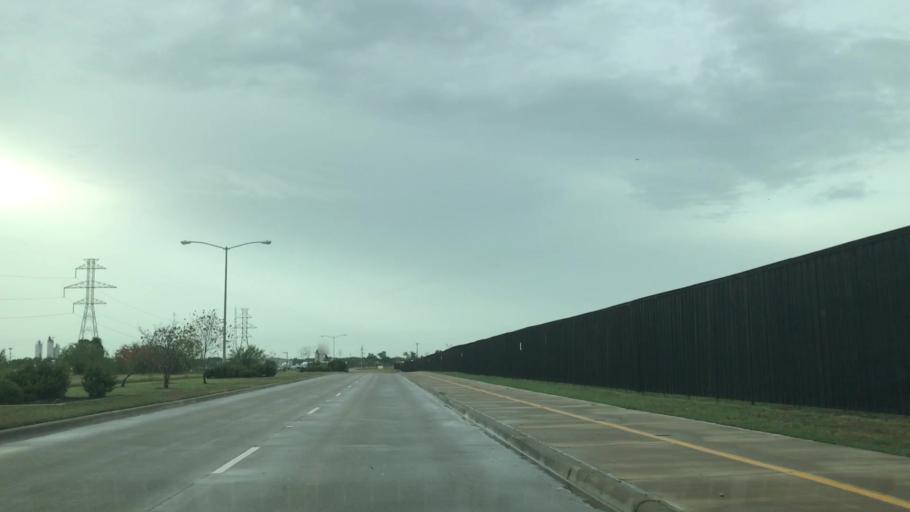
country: US
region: Texas
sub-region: Denton County
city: Lewisville
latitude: 33.0463
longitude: -96.9779
